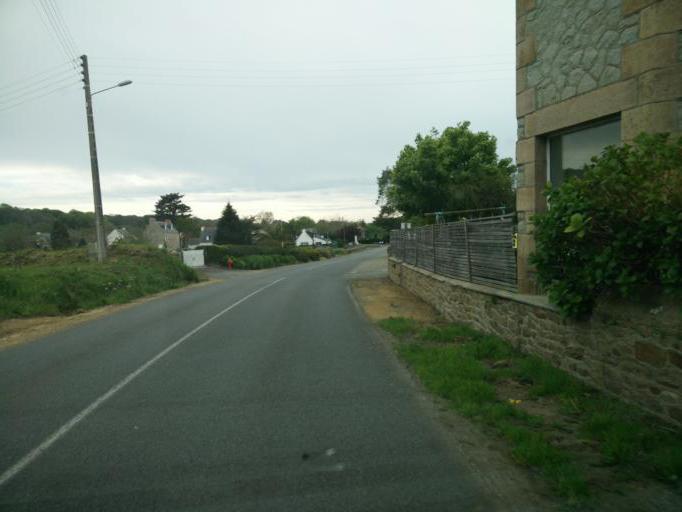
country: FR
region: Brittany
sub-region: Departement des Cotes-d'Armor
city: Trebeurden
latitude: 48.7919
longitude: -3.5529
